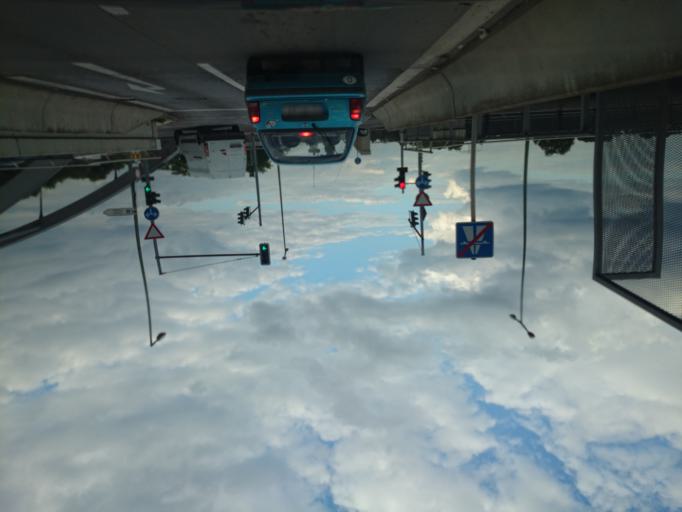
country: DE
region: Berlin
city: Rudow
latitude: 52.4431
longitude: 13.4784
